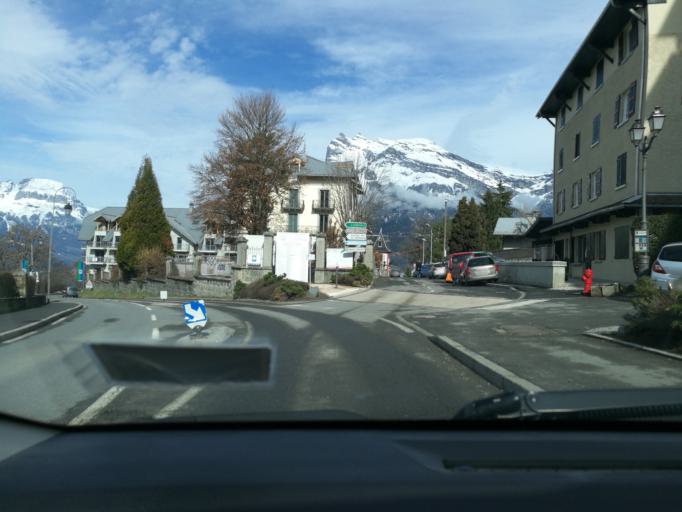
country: FR
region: Rhone-Alpes
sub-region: Departement de la Haute-Savoie
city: Saint-Gervais-les-Bains
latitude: 45.8964
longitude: 6.7103
